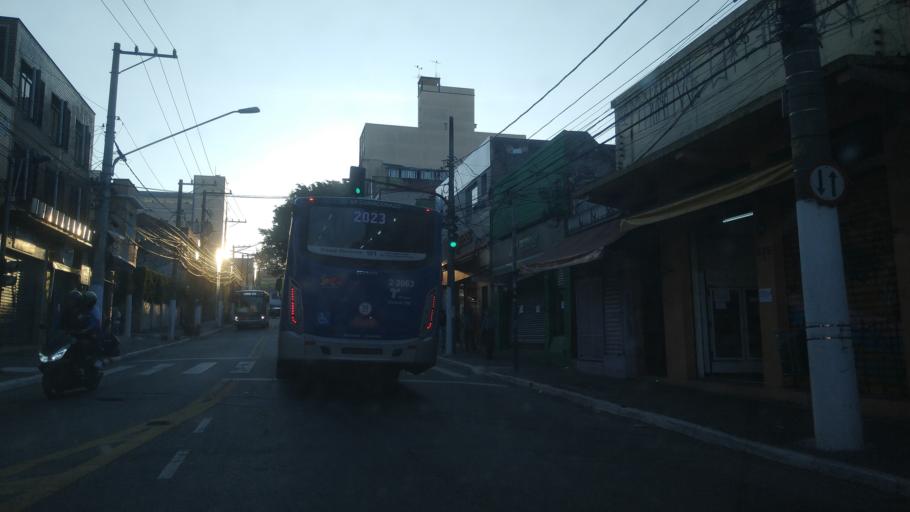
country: BR
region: Sao Paulo
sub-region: Sao Paulo
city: Sao Paulo
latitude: -23.4809
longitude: -46.6053
